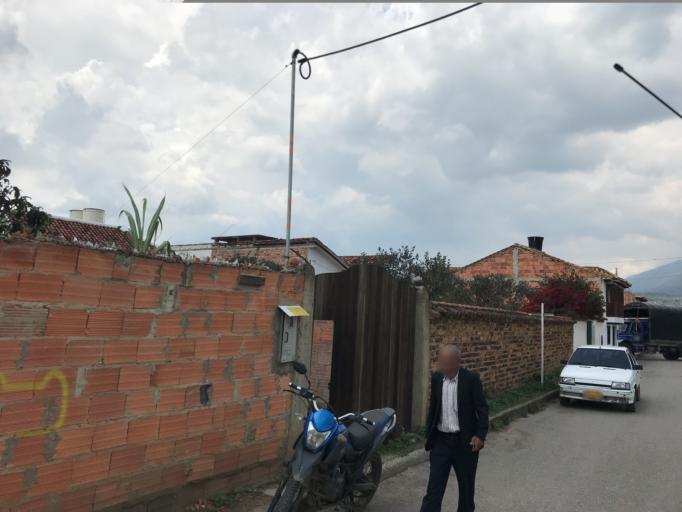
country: CO
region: Boyaca
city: Villa de Leiva
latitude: 5.6277
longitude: -73.5284
